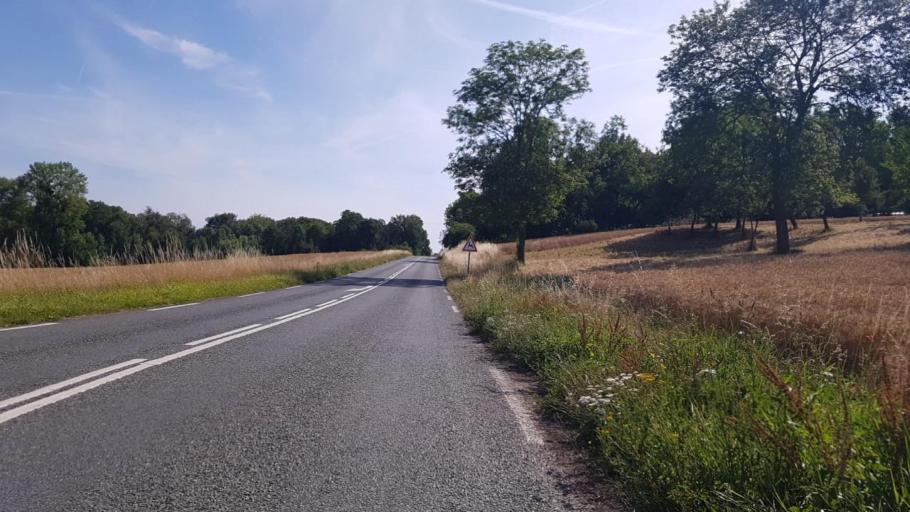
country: FR
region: Picardie
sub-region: Departement de l'Oise
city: Pontpoint
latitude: 49.3044
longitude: 2.6644
